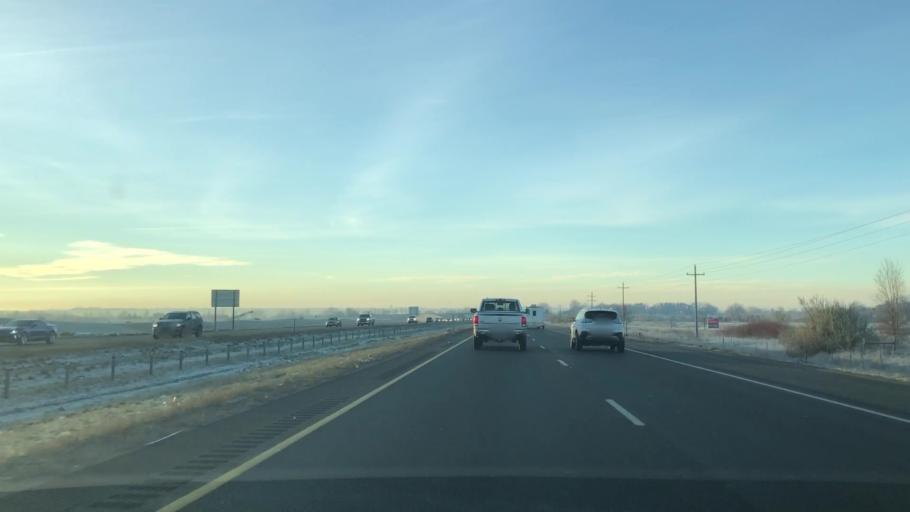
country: US
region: Colorado
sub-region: Weld County
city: Windsor
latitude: 40.5153
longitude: -104.9931
